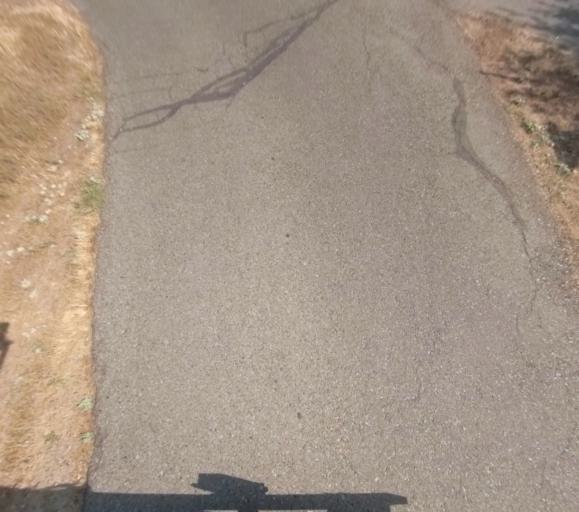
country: US
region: California
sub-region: Fresno County
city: Auberry
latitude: 37.2270
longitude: -119.5229
